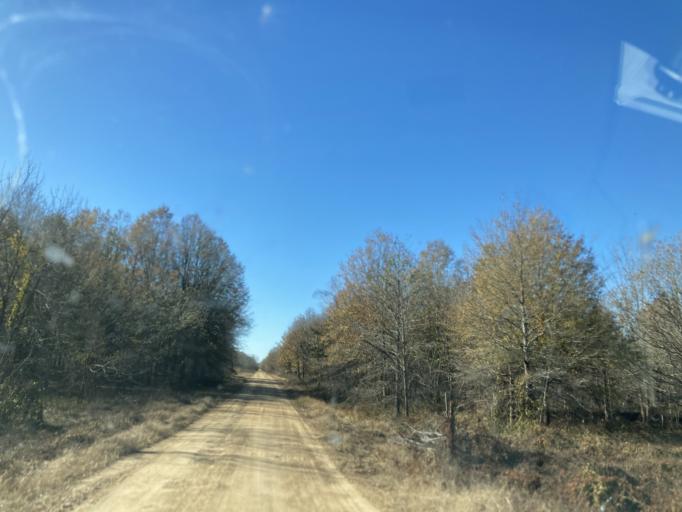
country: US
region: Mississippi
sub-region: Sharkey County
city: Rolling Fork
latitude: 32.7491
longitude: -90.6709
